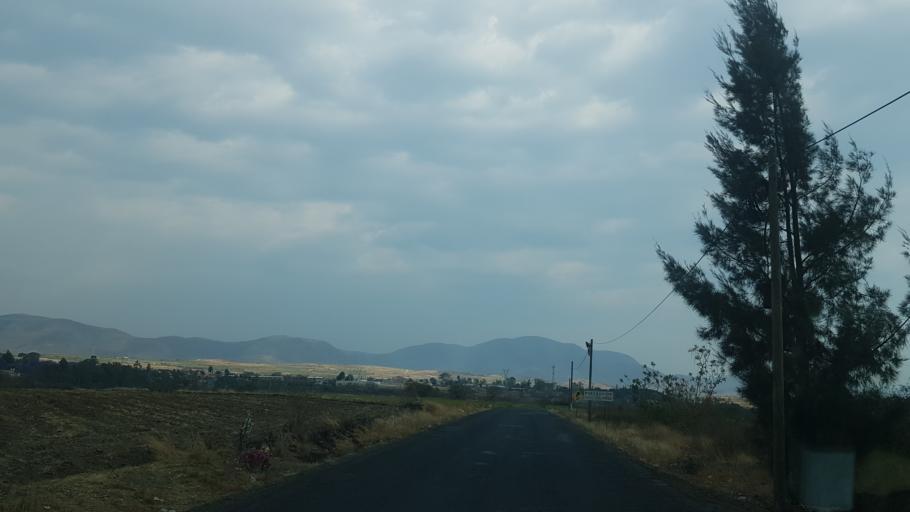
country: MX
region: Puebla
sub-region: Santa Isabel Cholula
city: Santa Ana Acozautla
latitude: 18.9578
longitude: -98.3944
